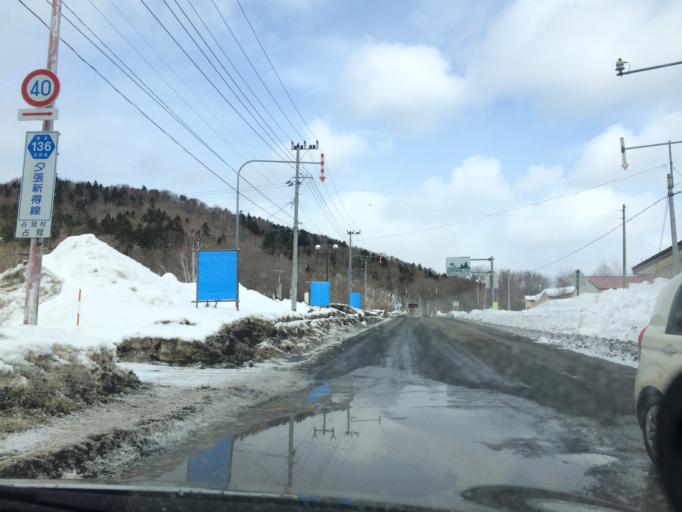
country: JP
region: Hokkaido
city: Shimo-furano
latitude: 43.0055
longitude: 142.4057
